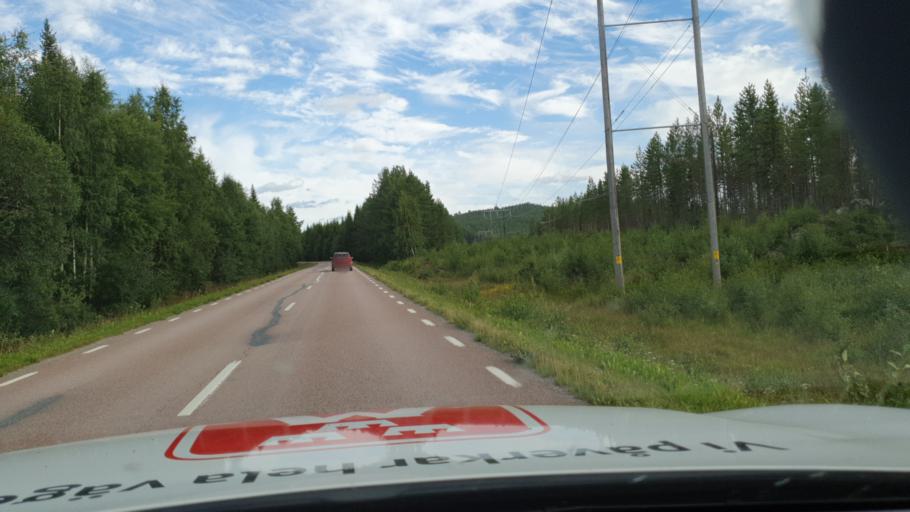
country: SE
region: Jaemtland
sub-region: Stroemsunds Kommun
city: Stroemsund
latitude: 63.6382
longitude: 16.0296
